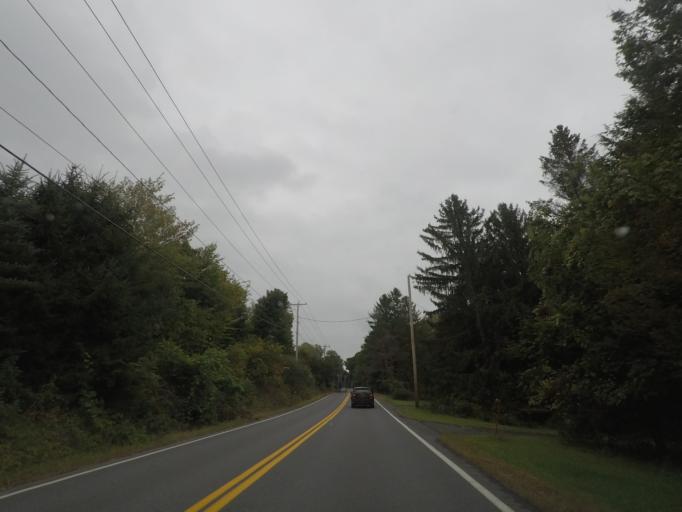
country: US
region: New York
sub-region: Rensselaer County
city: Hampton Manor
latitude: 42.6471
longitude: -73.6863
